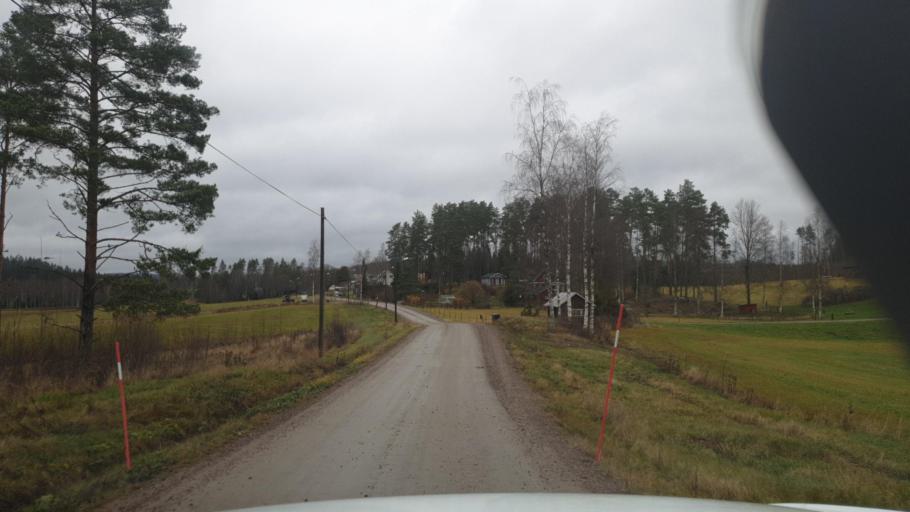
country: SE
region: Vaermland
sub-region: Arvika Kommun
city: Arvika
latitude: 59.8706
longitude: 12.6150
